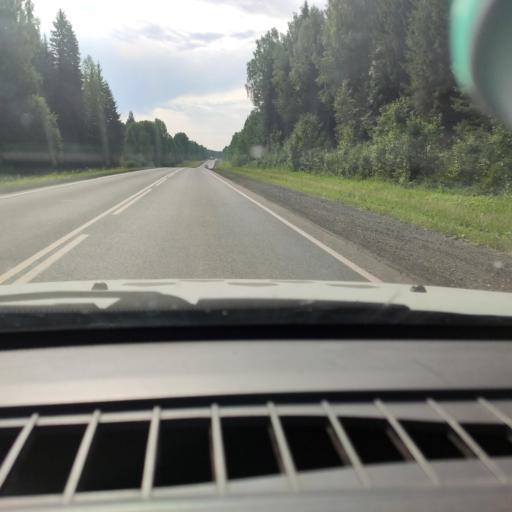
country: RU
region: Perm
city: Zyukayka
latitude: 58.3635
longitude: 54.6856
